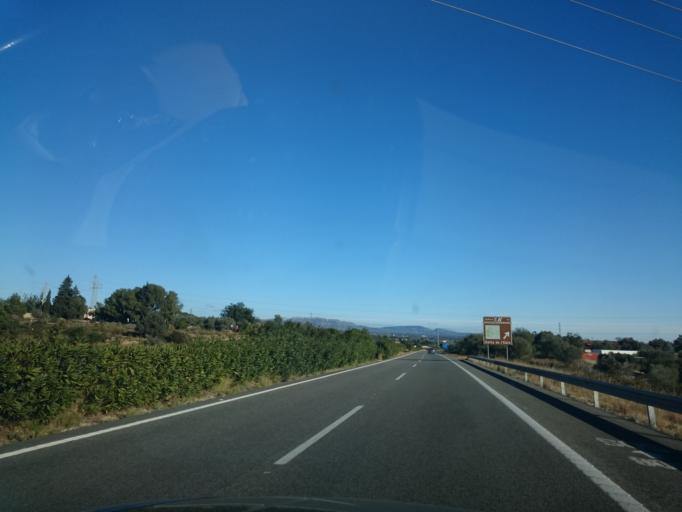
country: ES
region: Catalonia
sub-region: Provincia de Tarragona
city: Masdenverge
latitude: 40.7094
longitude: 0.5532
